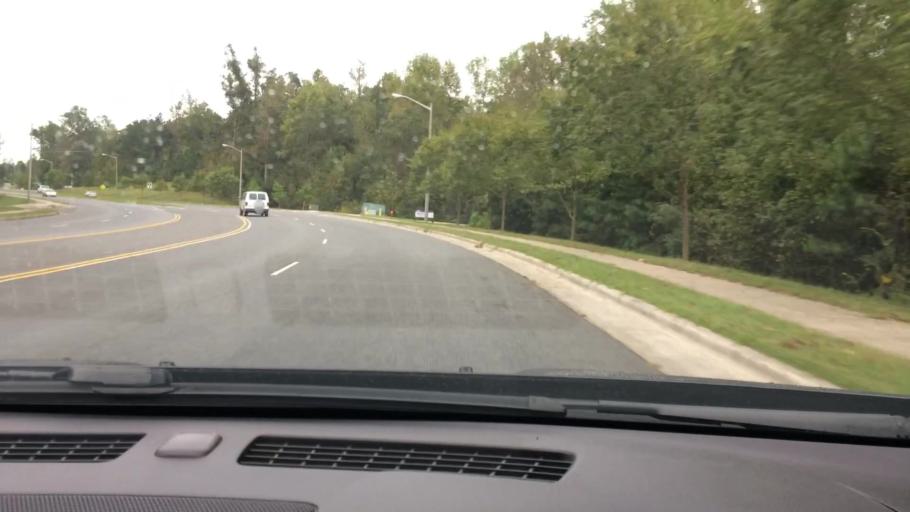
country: US
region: North Carolina
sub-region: Pitt County
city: Greenville
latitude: 35.6142
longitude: -77.4110
